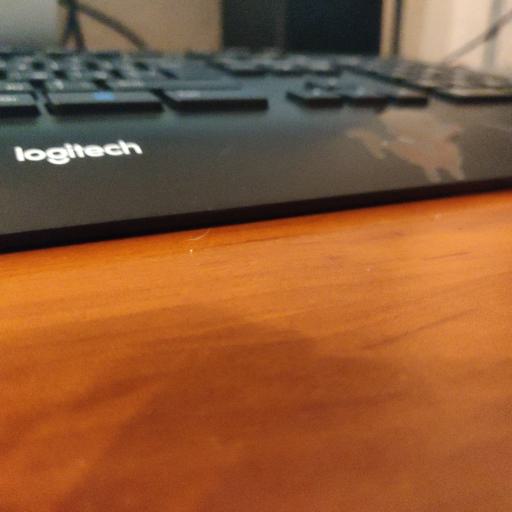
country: SE
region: Vaestmanland
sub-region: Vasteras
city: Tillberga
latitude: 59.7722
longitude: 16.5719
